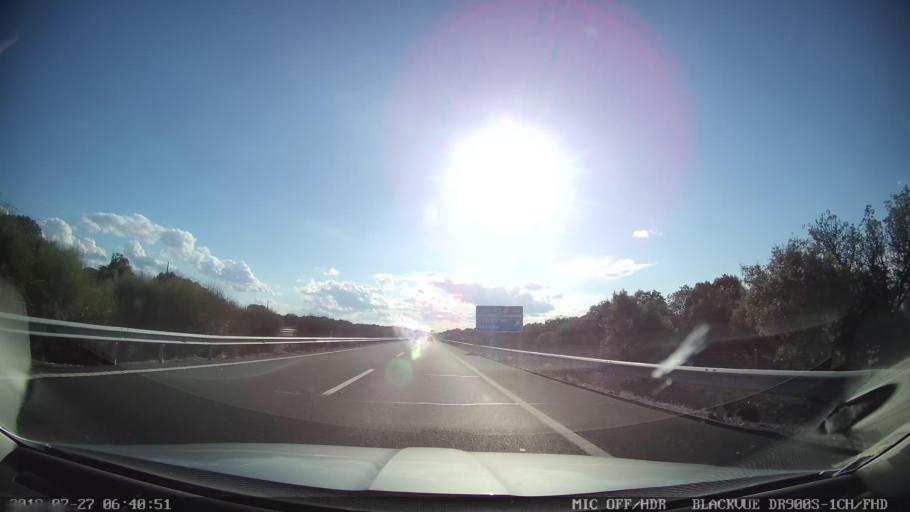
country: ES
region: Extremadura
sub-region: Provincia de Caceres
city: Peraleda de la Mata
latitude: 39.8897
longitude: -5.4507
